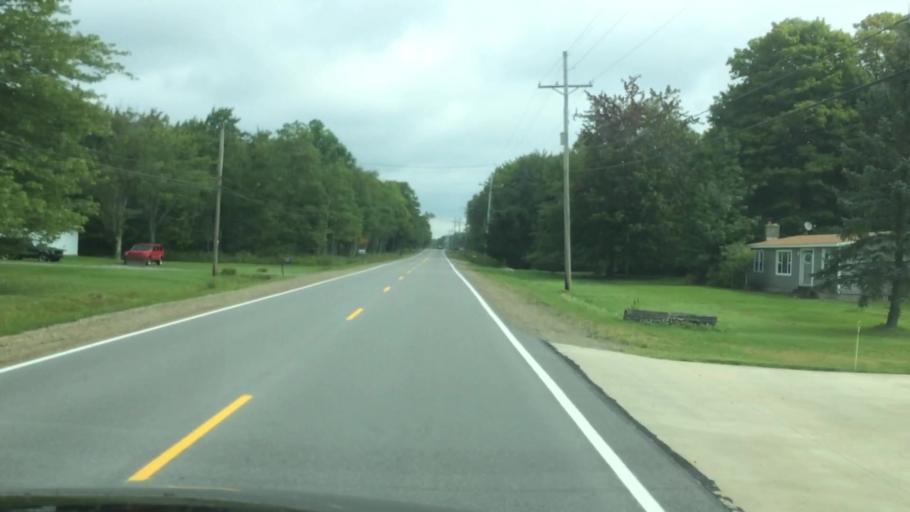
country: US
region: Pennsylvania
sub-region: McKean County
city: Bradford
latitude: 41.8735
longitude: -78.5859
